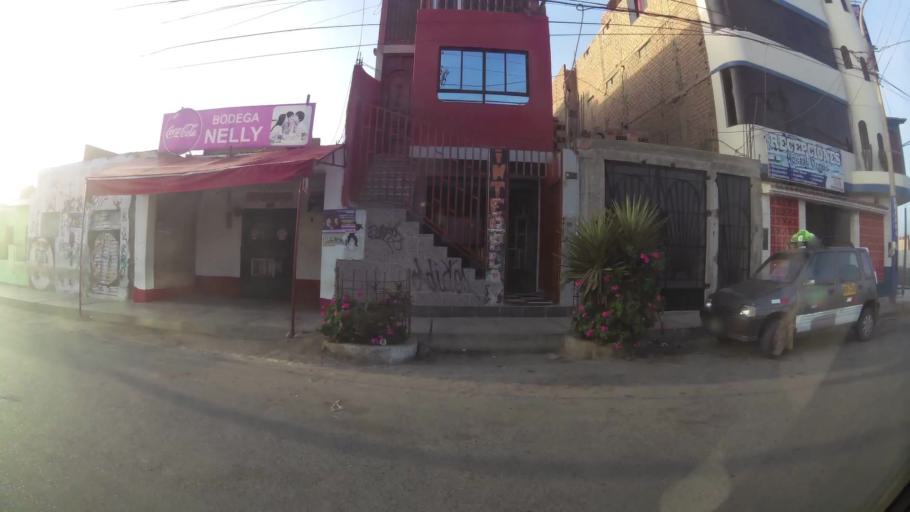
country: PE
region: Lima
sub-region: Huaura
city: Hualmay
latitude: -11.1006
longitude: -77.6120
